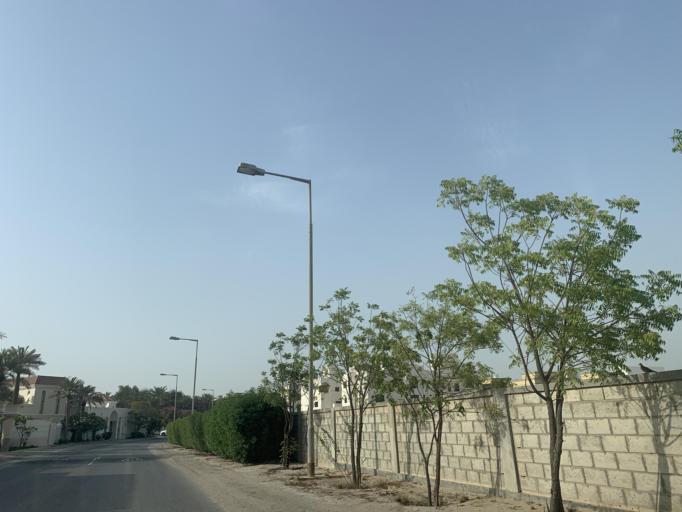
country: BH
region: Central Governorate
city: Madinat Hamad
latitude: 26.1775
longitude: 50.4761
